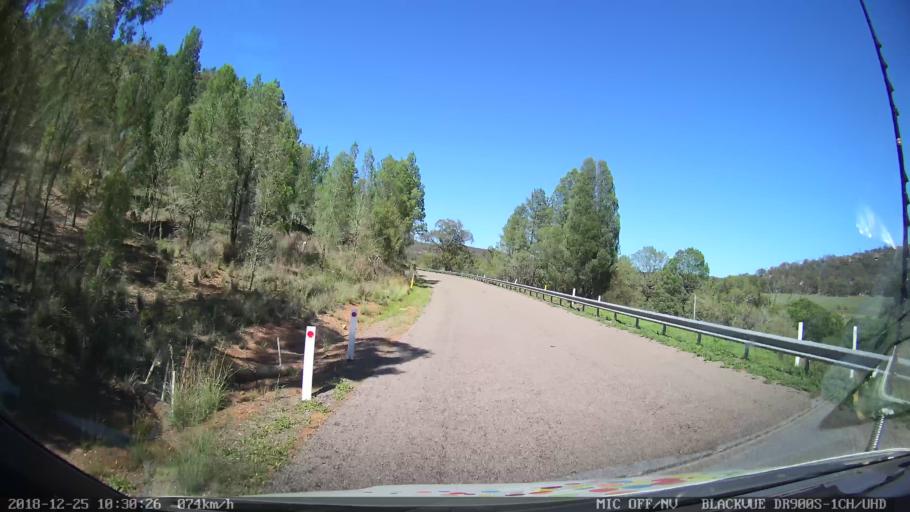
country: AU
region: New South Wales
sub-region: Muswellbrook
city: Denman
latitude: -32.3820
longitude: 150.4378
